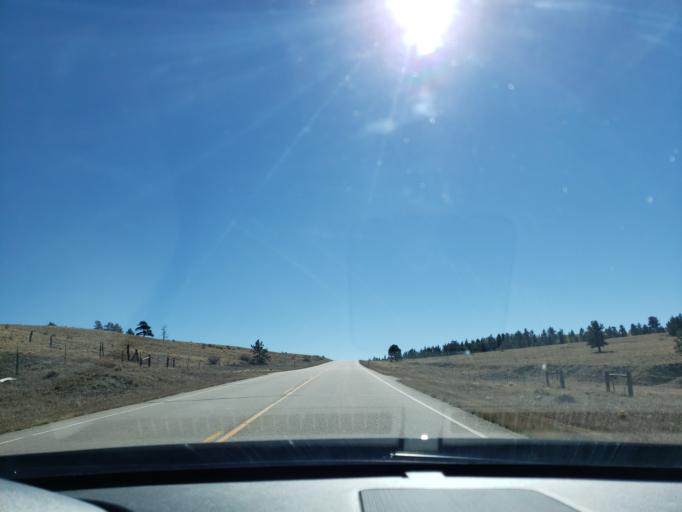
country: US
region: Colorado
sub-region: Park County
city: Fairplay
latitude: 38.9125
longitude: -105.7028
